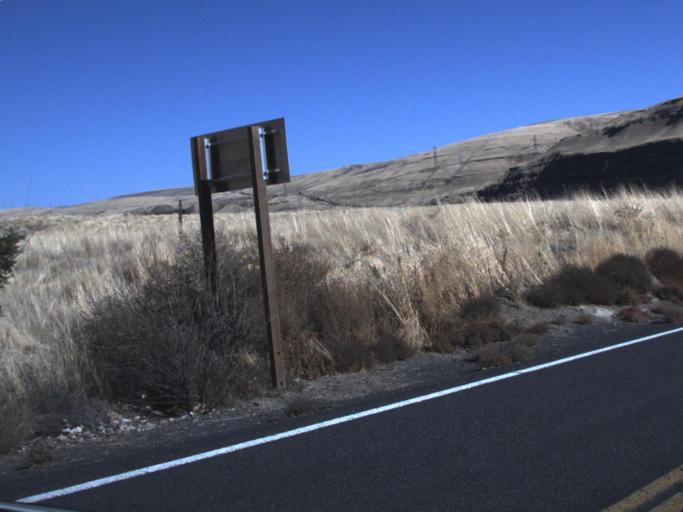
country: US
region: Washington
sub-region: Franklin County
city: Connell
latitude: 46.5355
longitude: -118.5752
